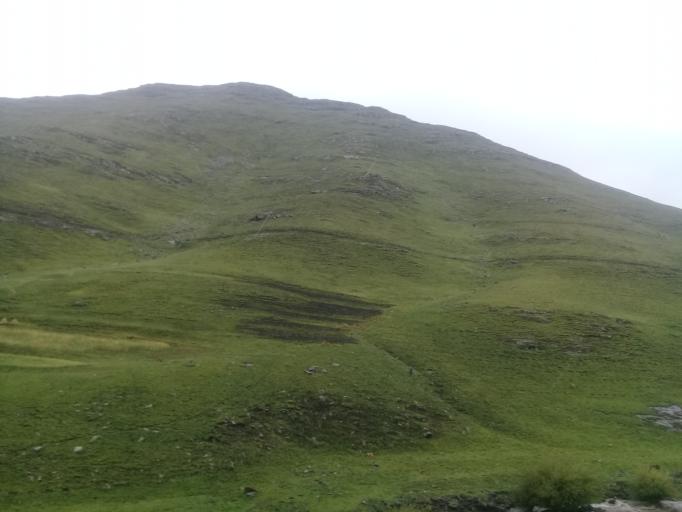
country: LS
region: Mokhotlong
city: Mokhotlong
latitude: -29.3904
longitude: 28.9645
